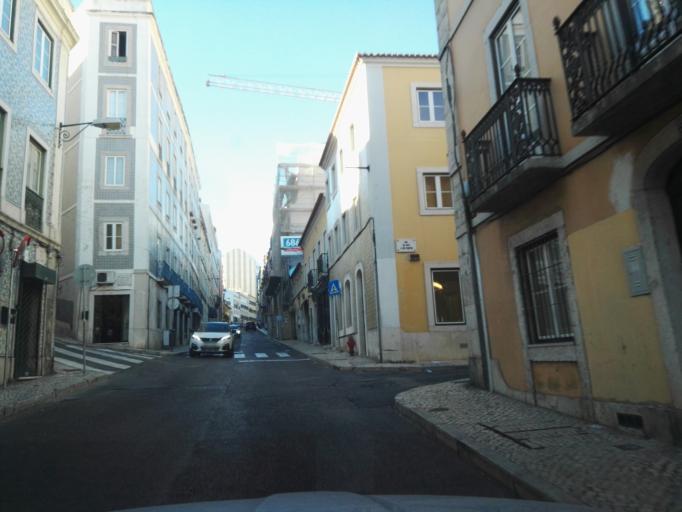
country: PT
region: Lisbon
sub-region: Lisbon
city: Lisbon
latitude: 38.7169
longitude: -9.1551
